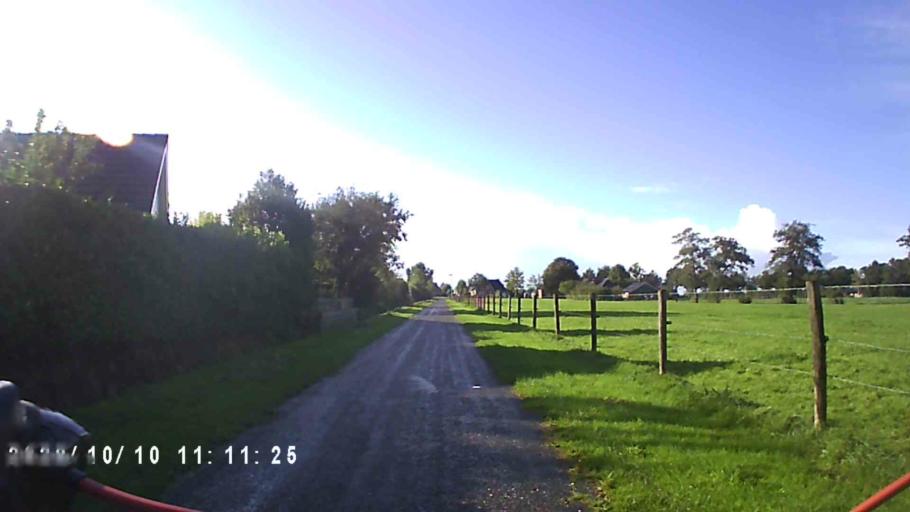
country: NL
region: Friesland
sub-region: Gemeente Smallingerland
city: Drachtstercompagnie
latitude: 53.1136
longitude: 6.2058
